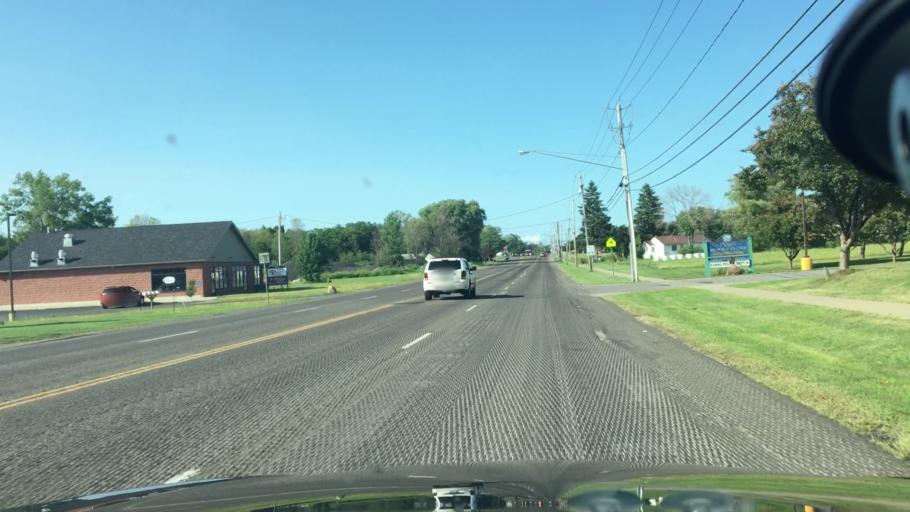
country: US
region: New York
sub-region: Erie County
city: Angola on the Lake
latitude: 42.6465
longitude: -79.0430
